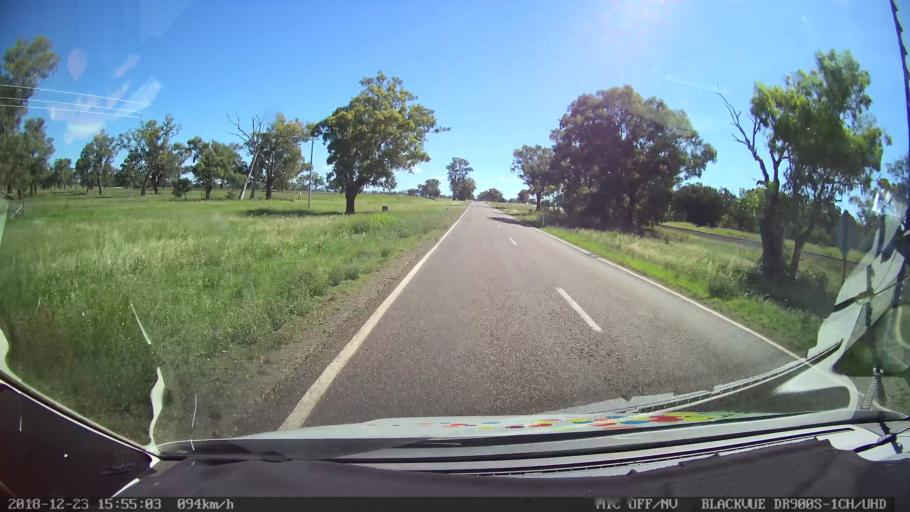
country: AU
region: New South Wales
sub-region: Tamworth Municipality
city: Phillip
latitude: -31.1514
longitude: 150.8724
